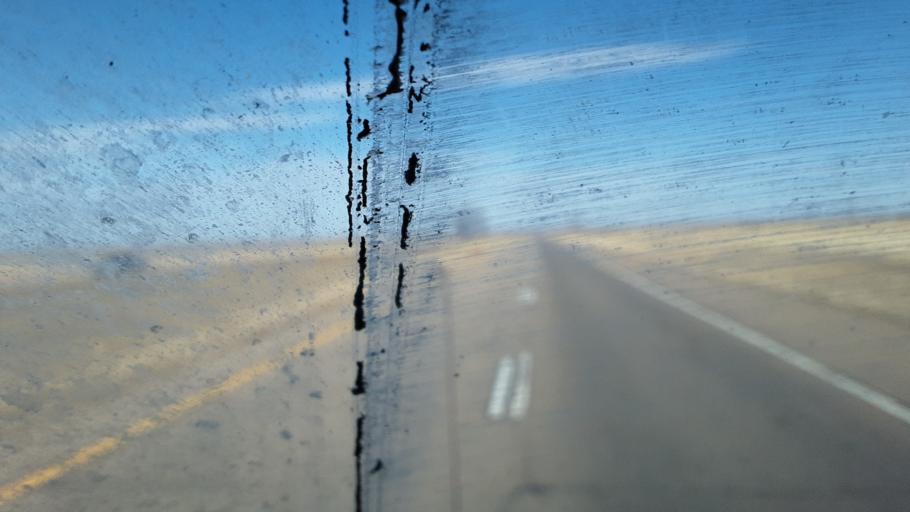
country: US
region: Colorado
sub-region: Weld County
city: Keenesburg
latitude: 40.1401
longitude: -104.4777
